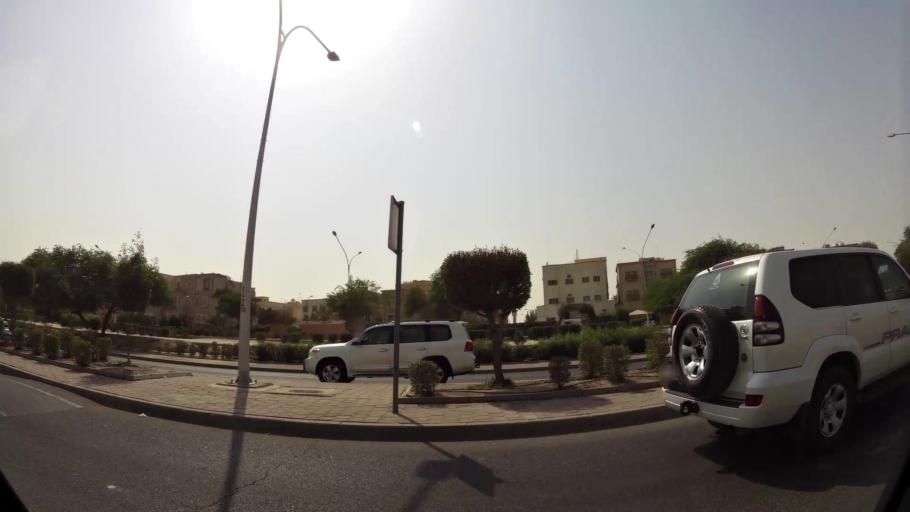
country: KW
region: Muhafazat al Jahra'
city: Al Jahra'
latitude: 29.3354
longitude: 47.6982
